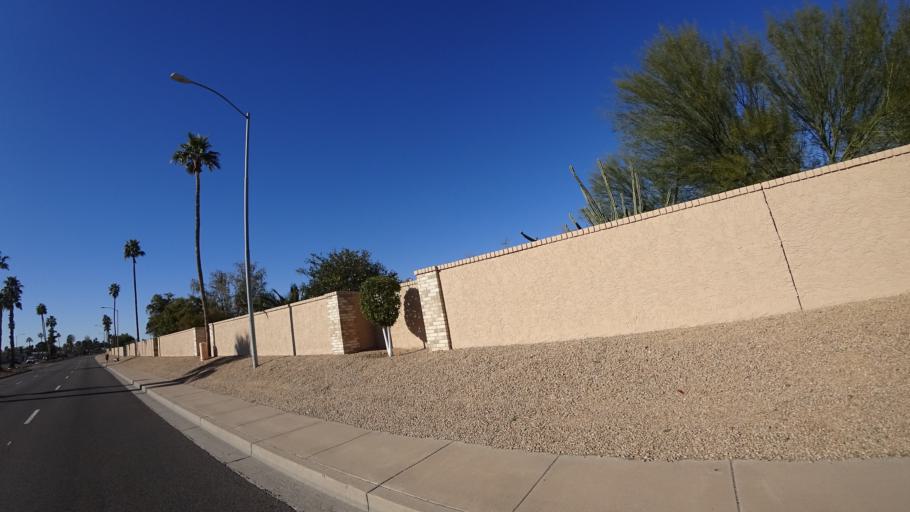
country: US
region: Arizona
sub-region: Maricopa County
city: Sun City West
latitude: 33.6519
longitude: -112.3416
